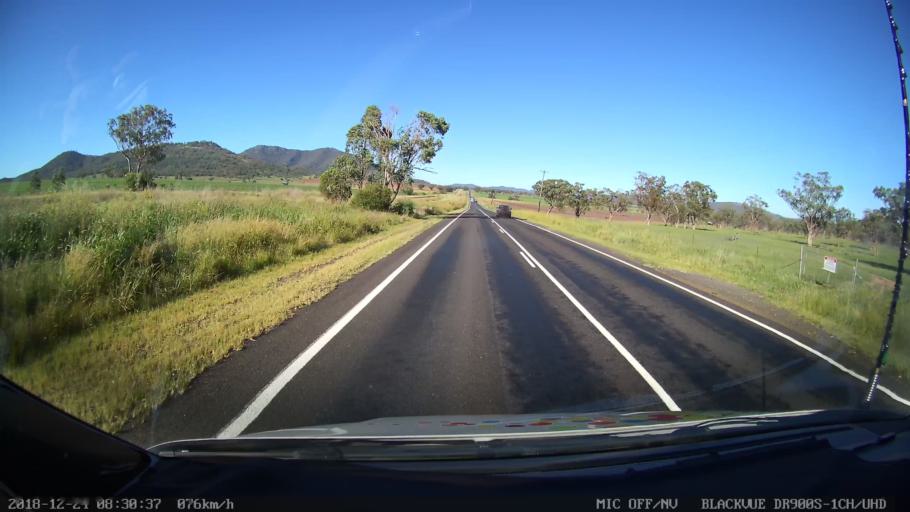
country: AU
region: New South Wales
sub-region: Tamworth Municipality
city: Phillip
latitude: -31.2685
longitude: 150.7223
